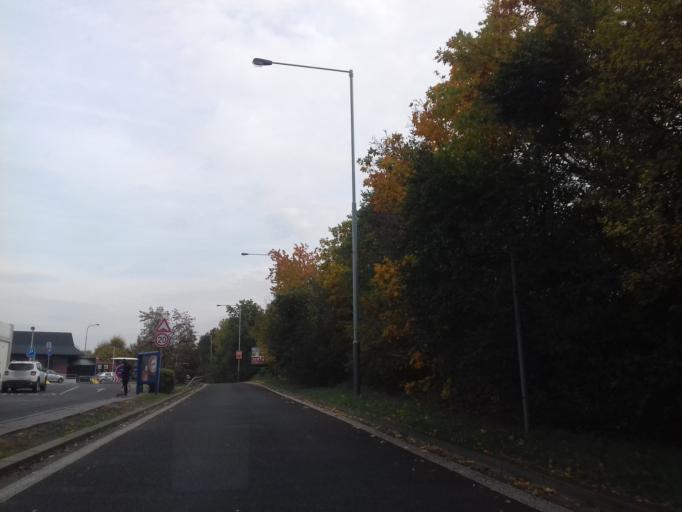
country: CZ
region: Praha
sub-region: Praha 4
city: Hodkovicky
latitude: 50.0334
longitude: 14.4412
